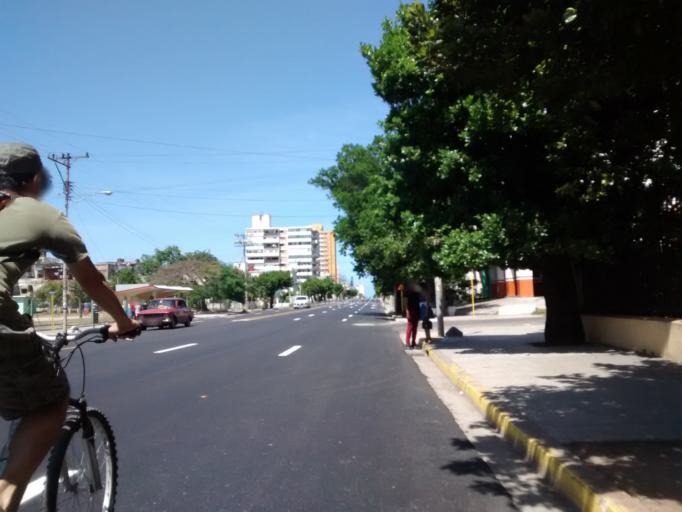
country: CU
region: La Habana
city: Havana
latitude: 23.1325
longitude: -82.3925
